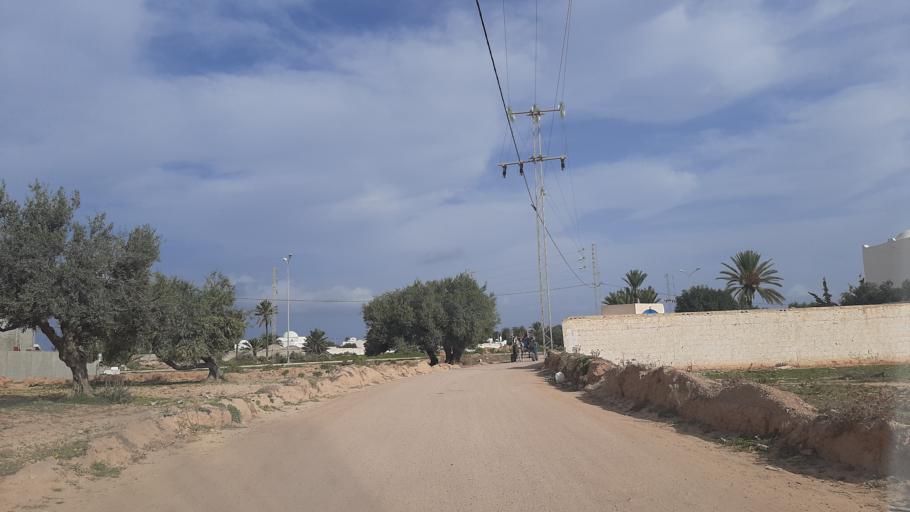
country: TN
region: Madanin
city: Midoun
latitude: 33.8173
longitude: 11.0258
